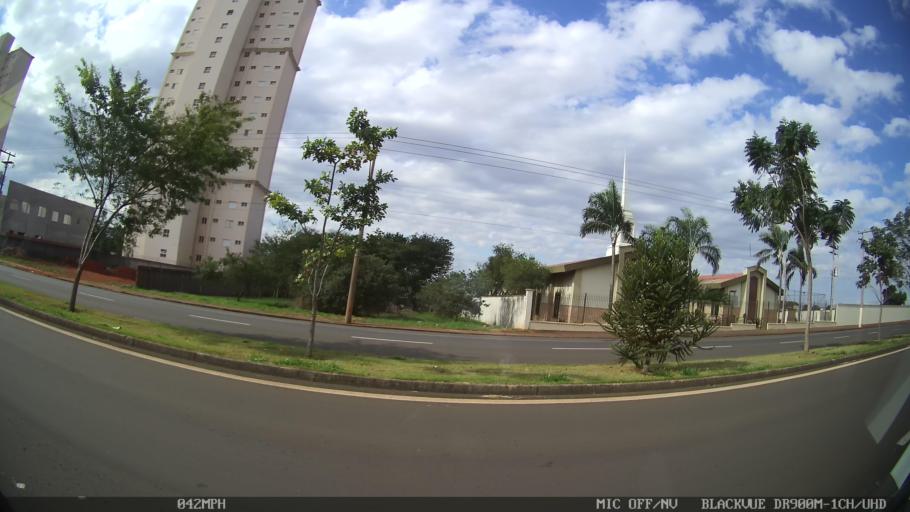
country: BR
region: Sao Paulo
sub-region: Limeira
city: Limeira
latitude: -22.5552
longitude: -47.4253
